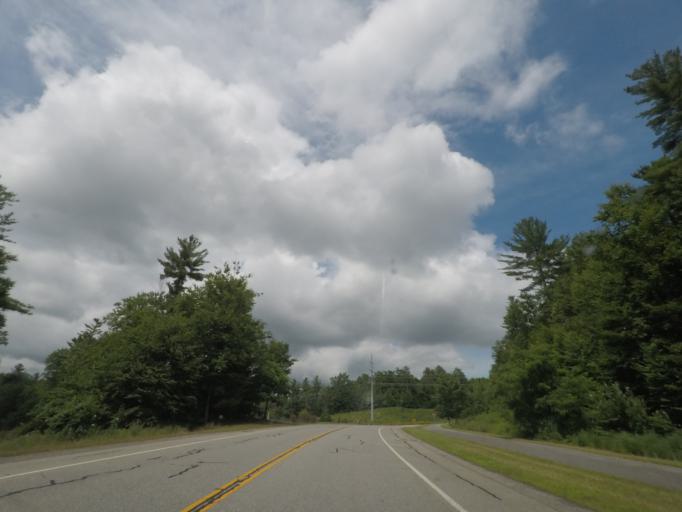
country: US
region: New York
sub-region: Saratoga County
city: Country Knolls
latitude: 42.9576
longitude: -73.7768
